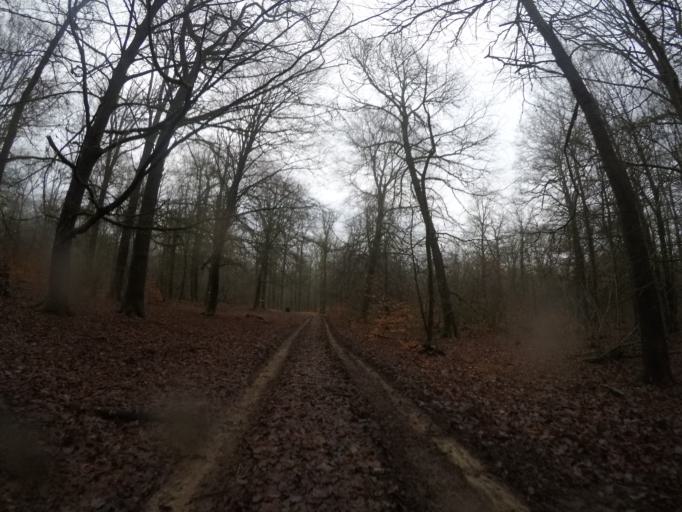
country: BE
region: Wallonia
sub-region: Province du Luxembourg
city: Leglise
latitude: 49.8143
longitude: 5.6020
